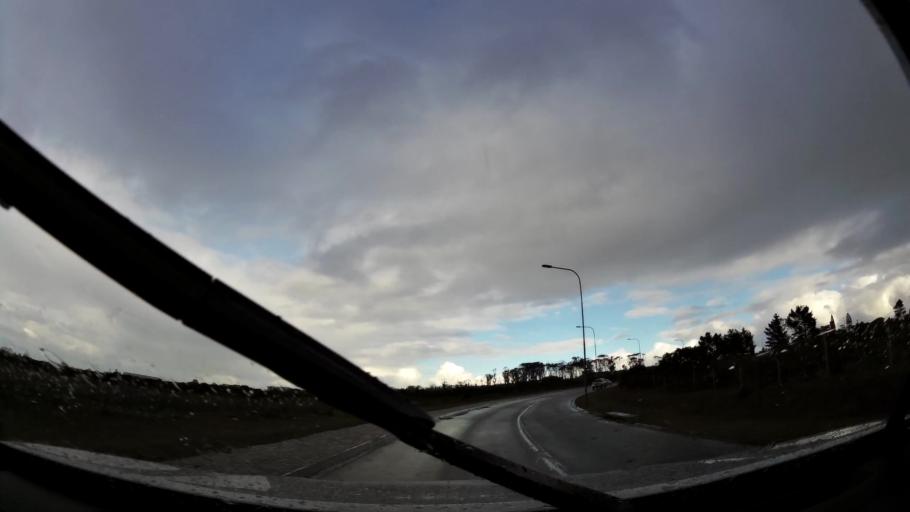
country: ZA
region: Western Cape
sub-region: Eden District Municipality
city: Mossel Bay
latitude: -34.1843
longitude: 22.0921
